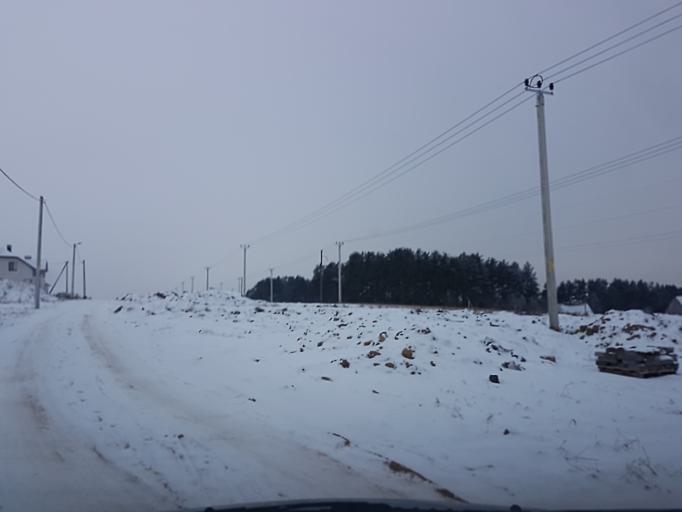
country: BY
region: Minsk
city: Rakaw
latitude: 53.9634
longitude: 27.0346
